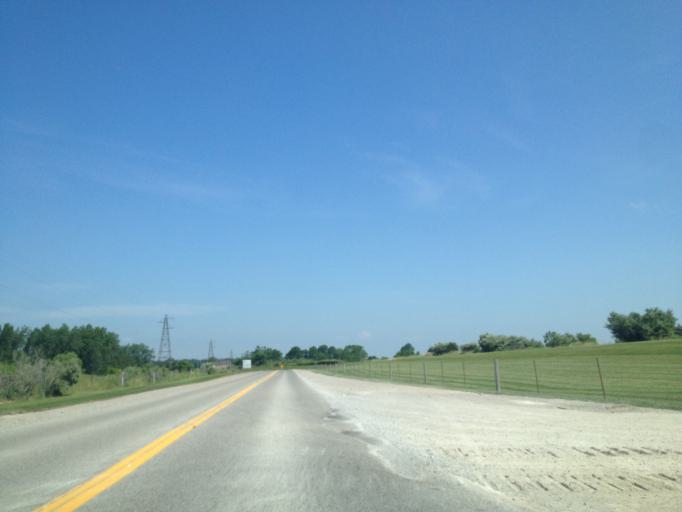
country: CA
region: Ontario
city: London
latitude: 43.0665
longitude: -81.2064
